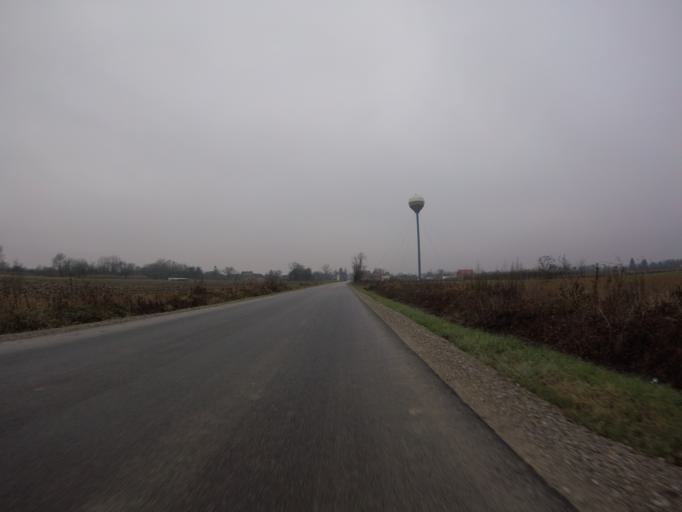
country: HR
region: Sisacko-Moslavacka
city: Lekenik
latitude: 45.6497
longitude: 16.2713
